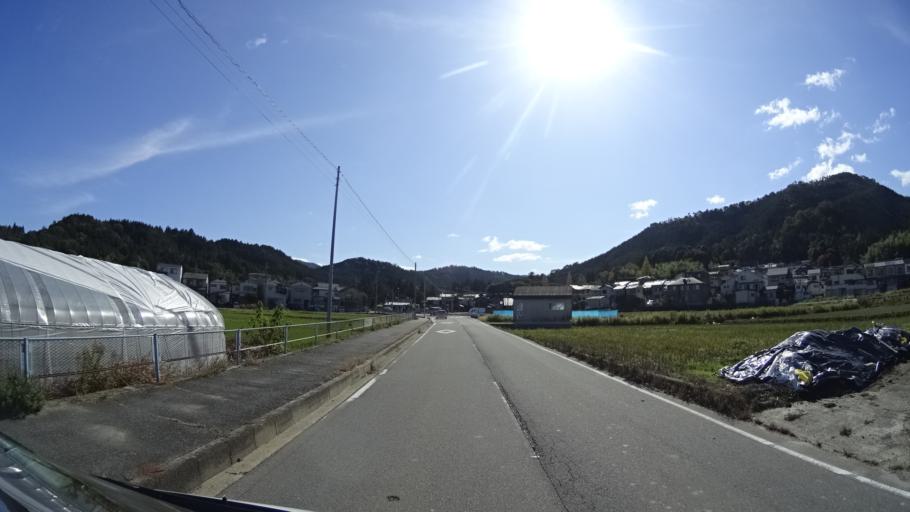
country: JP
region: Kyoto
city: Kameoka
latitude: 34.9991
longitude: 135.5782
